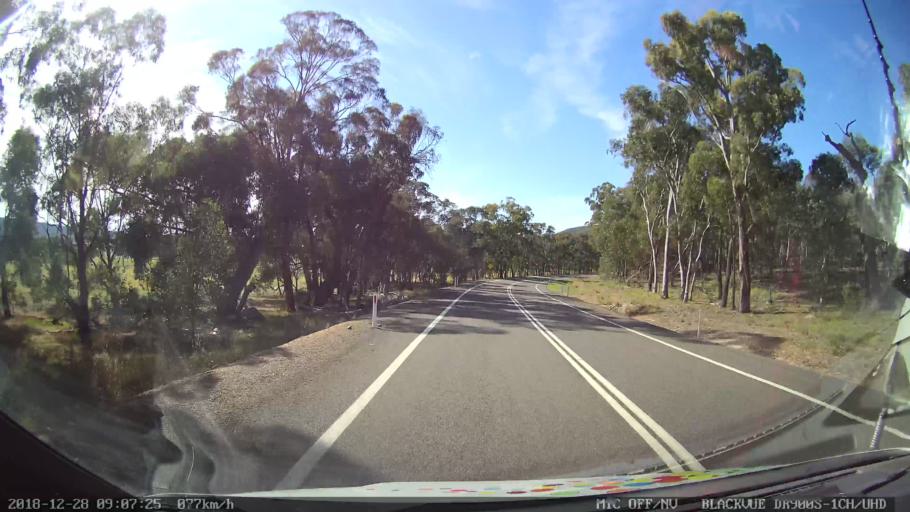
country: AU
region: New South Wales
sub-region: Upper Lachlan Shire
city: Crookwell
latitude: -34.2064
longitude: 149.3450
